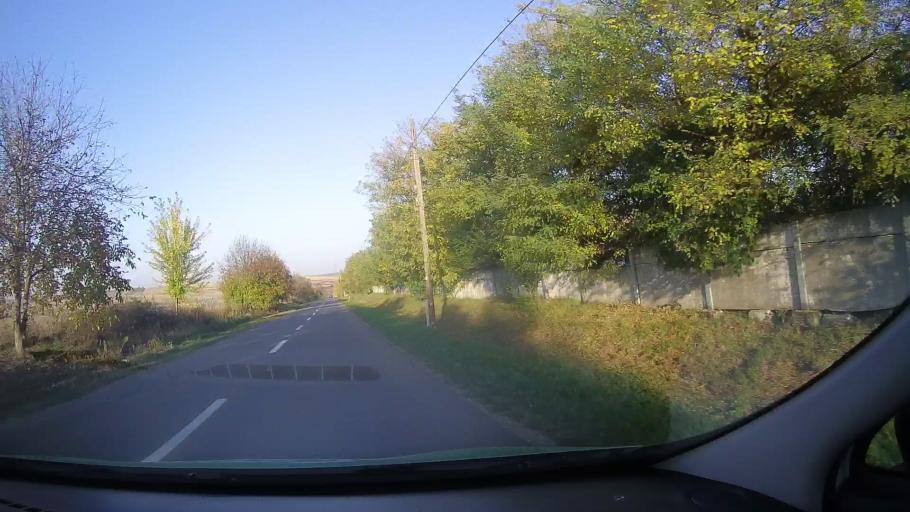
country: RO
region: Bihor
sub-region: Comuna Paleu
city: Paleu
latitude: 47.1162
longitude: 21.9462
